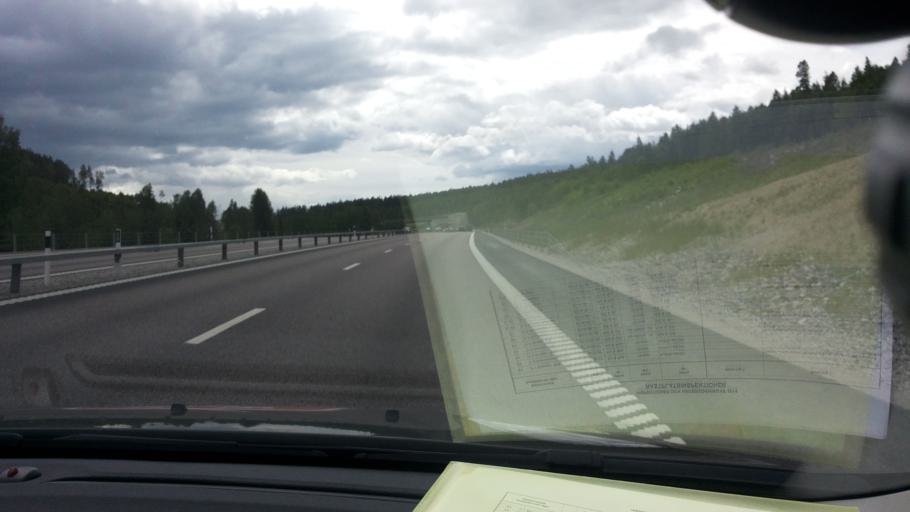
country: SE
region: Vaesternorrland
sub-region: Sundsvalls Kommun
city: Stockvik
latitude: 62.3266
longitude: 17.3451
